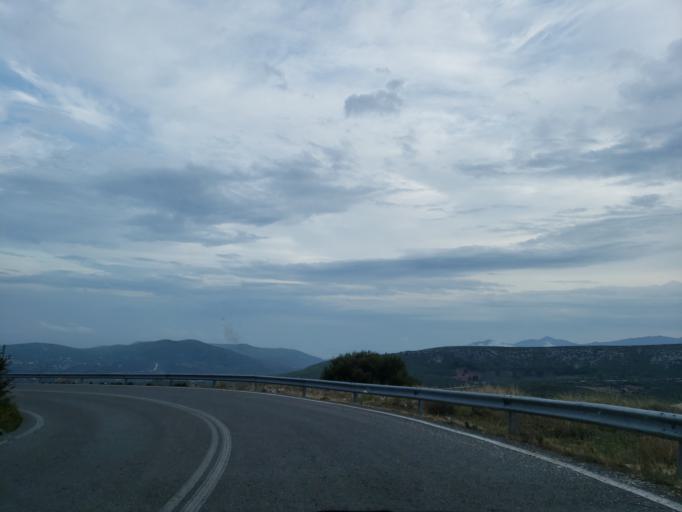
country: GR
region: Attica
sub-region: Nomarchia Anatolikis Attikis
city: Grammatiko
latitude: 38.2069
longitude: 23.9510
